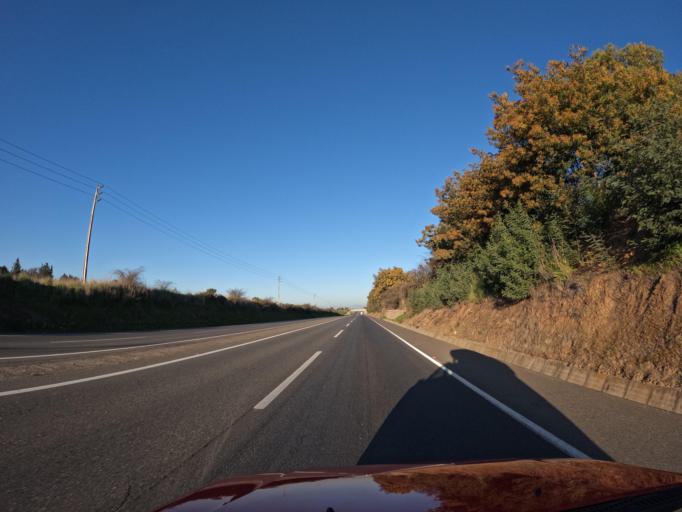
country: CL
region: Biobio
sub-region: Provincia de Nuble
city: Bulnes
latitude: -36.6588
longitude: -72.2893
